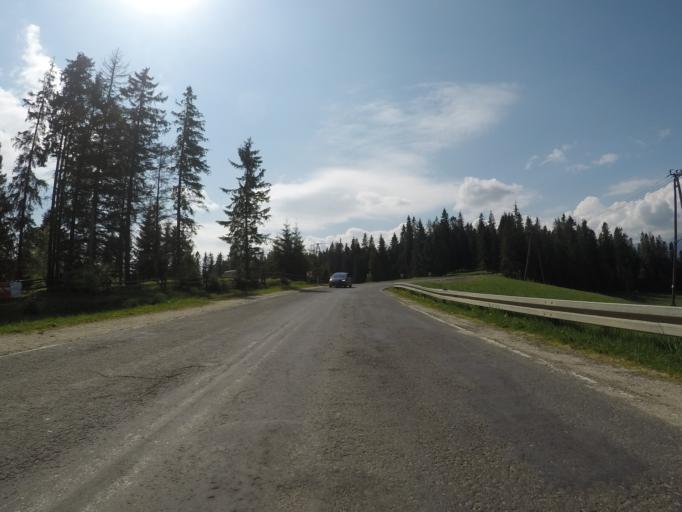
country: PL
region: Lesser Poland Voivodeship
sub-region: Powiat tatrzanski
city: Bukowina Tatrzanska
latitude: 49.3207
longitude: 20.1062
